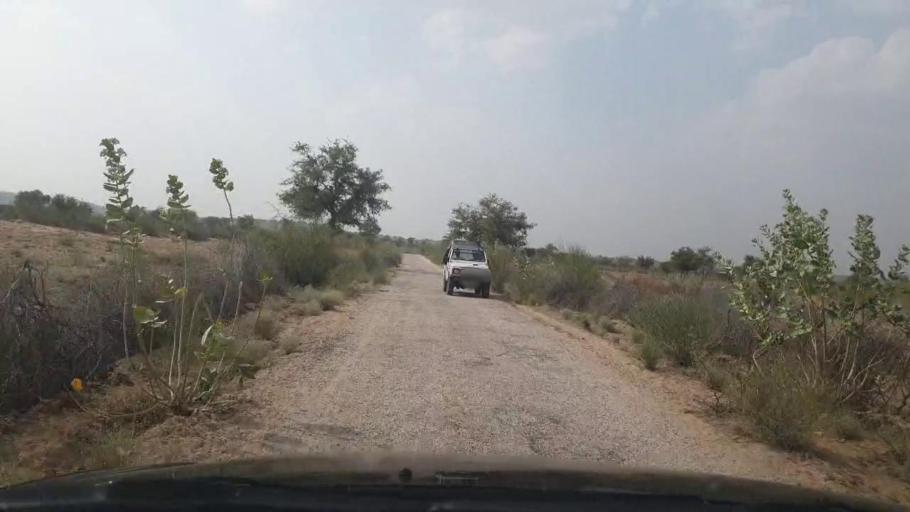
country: PK
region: Sindh
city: Islamkot
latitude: 24.9642
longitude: 70.6259
